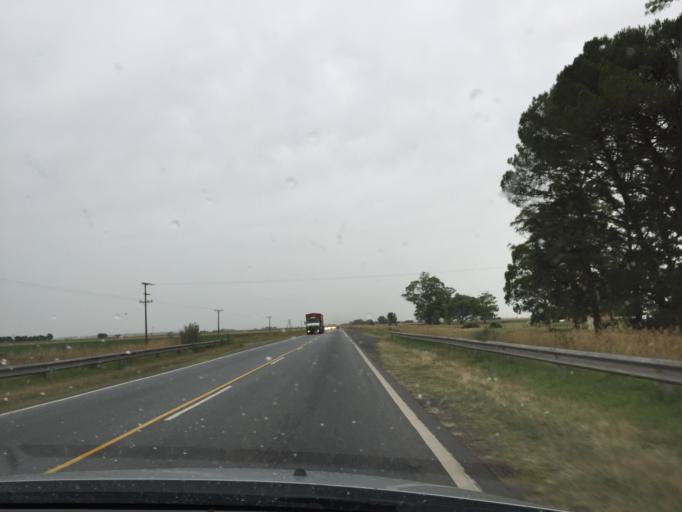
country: AR
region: Buenos Aires
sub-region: Partido de Tandil
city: Tandil
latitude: -37.5564
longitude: -58.7954
